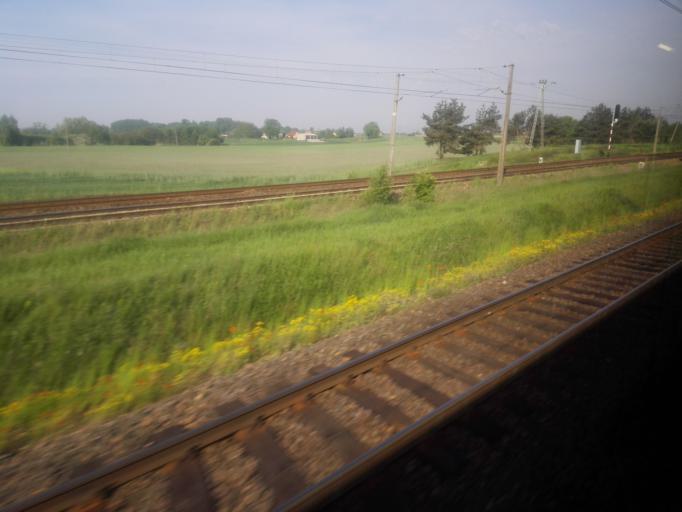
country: PL
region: Greater Poland Voivodeship
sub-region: Powiat wrzesinski
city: Wrzesnia
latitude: 52.3367
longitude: 17.4967
